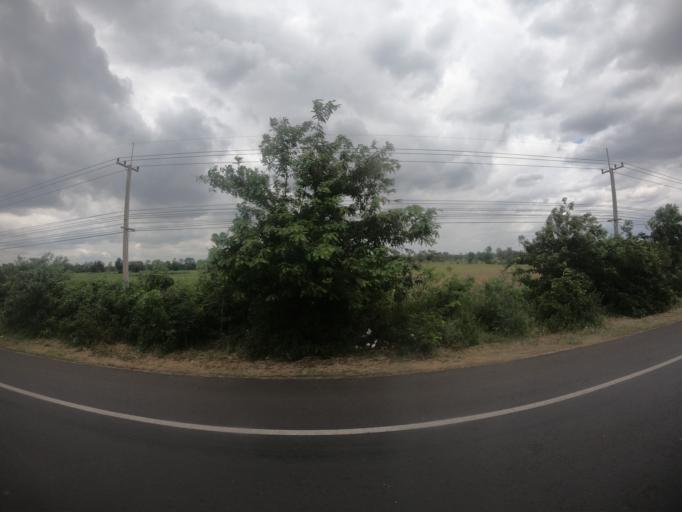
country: TH
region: Buriram
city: Nong Ki
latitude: 14.6781
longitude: 102.5615
